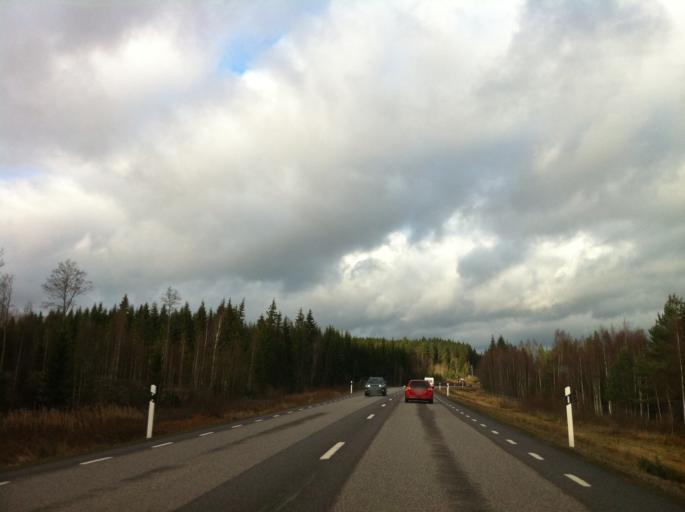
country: SE
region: Kalmar
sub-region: Vimmerby Kommun
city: Vimmerby
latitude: 57.6041
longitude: 15.8450
